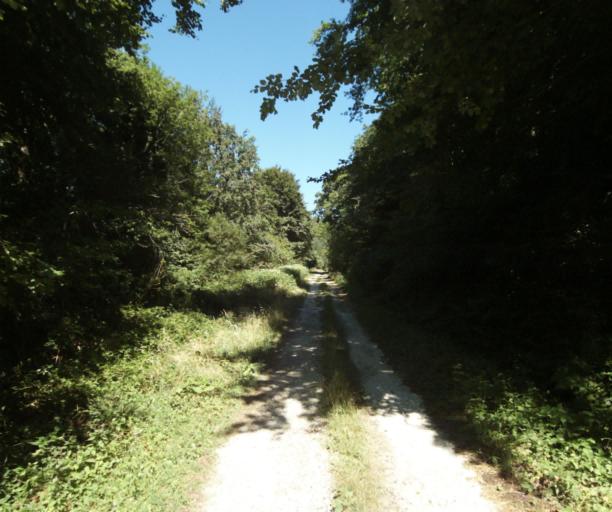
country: FR
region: Midi-Pyrenees
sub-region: Departement du Tarn
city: Soreze
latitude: 43.4380
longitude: 2.0979
